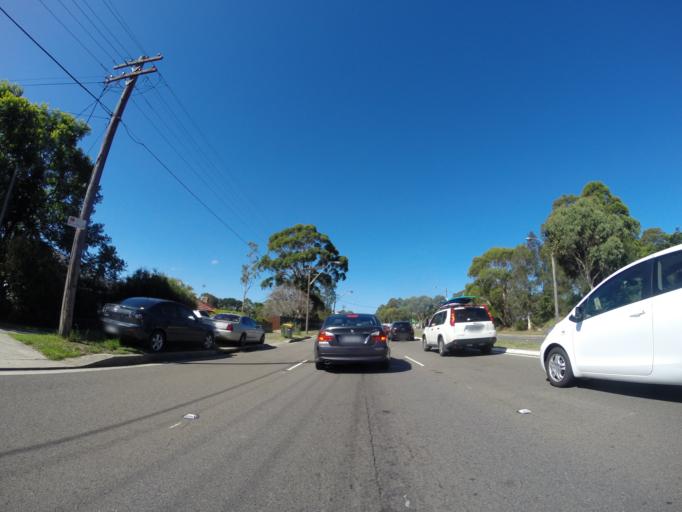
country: AU
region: New South Wales
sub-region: Sutherland Shire
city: Heathcote
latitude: -34.0890
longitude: 151.0060
